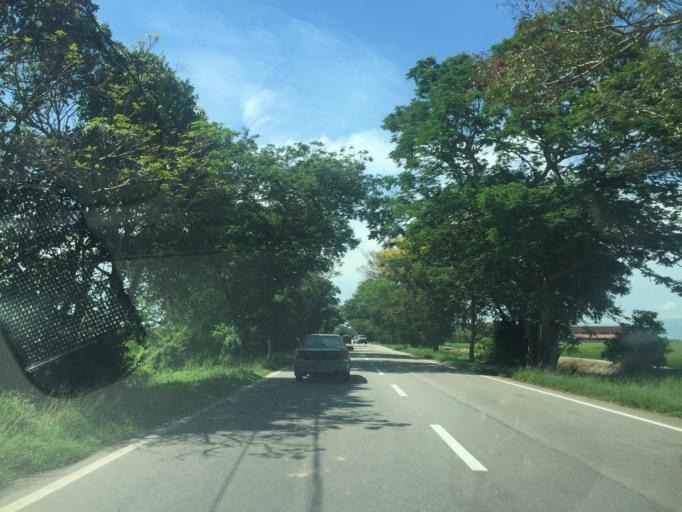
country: MY
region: Penang
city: Tasek Glugor
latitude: 5.4637
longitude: 100.4519
